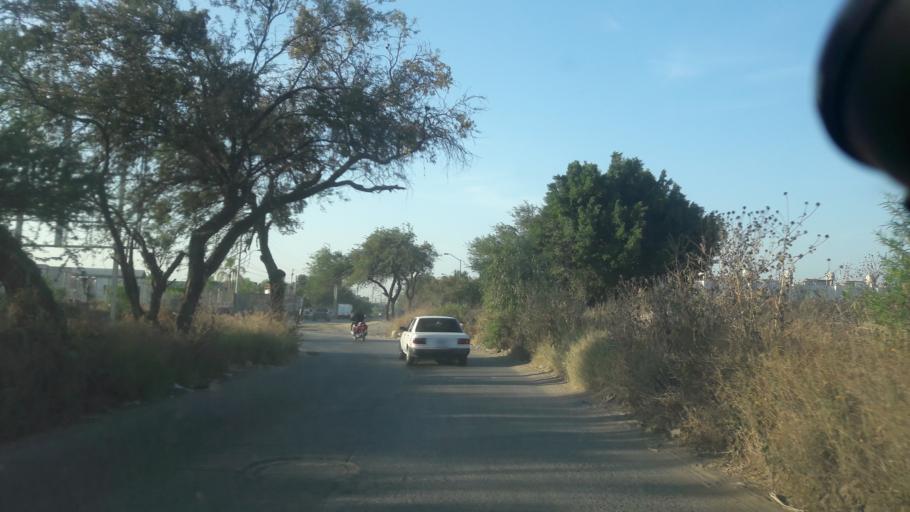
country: MX
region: Guanajuato
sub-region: Leon
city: Medina
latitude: 21.1682
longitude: -101.6406
